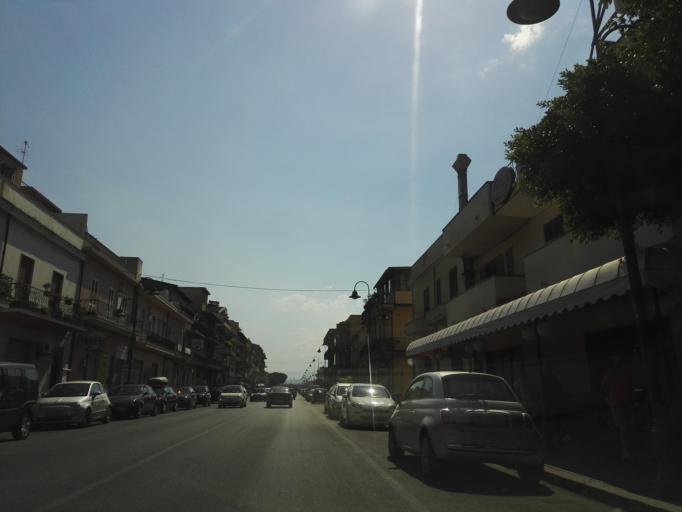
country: IT
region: Calabria
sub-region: Provincia di Reggio Calabria
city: Marina di Gioiosa Ionica
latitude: 38.2997
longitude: 16.3287
